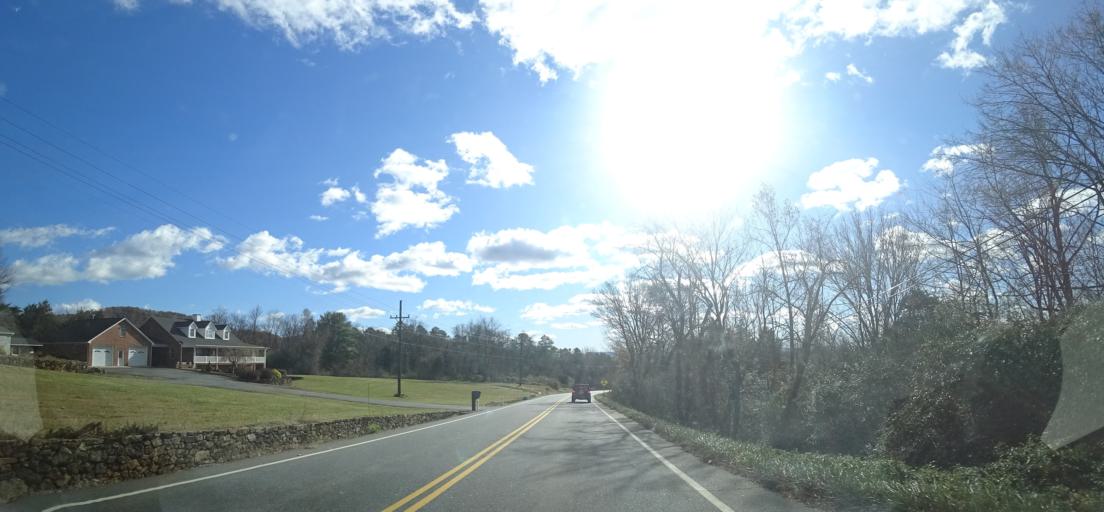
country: US
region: Virginia
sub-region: Greene County
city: Stanardsville
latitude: 38.3139
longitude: -78.4749
